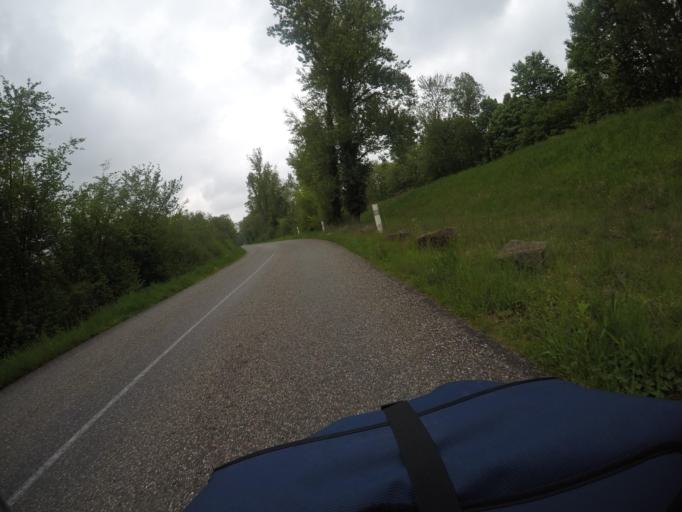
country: DE
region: Baden-Wuerttemberg
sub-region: Karlsruhe Region
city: Hugelsheim
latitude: 48.8399
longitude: 8.1040
